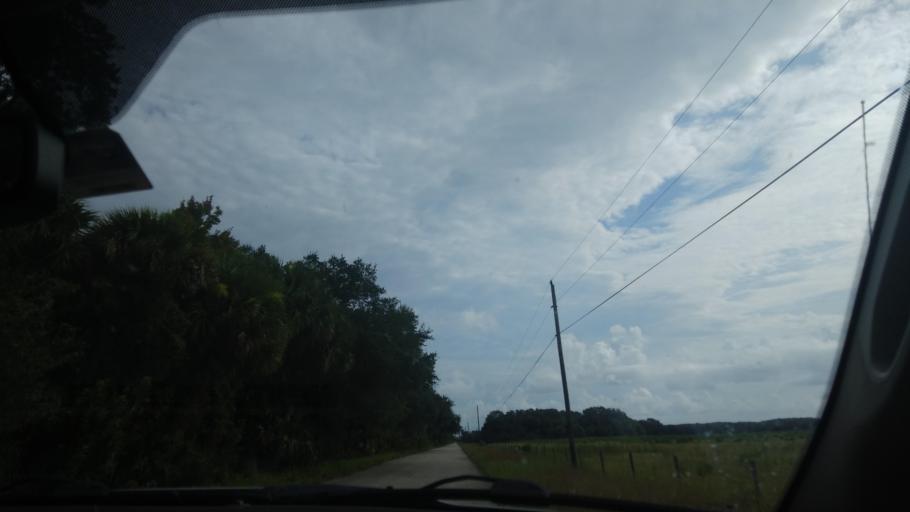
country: US
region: Florida
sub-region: Indian River County
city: Fellsmere
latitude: 27.6991
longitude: -80.7866
